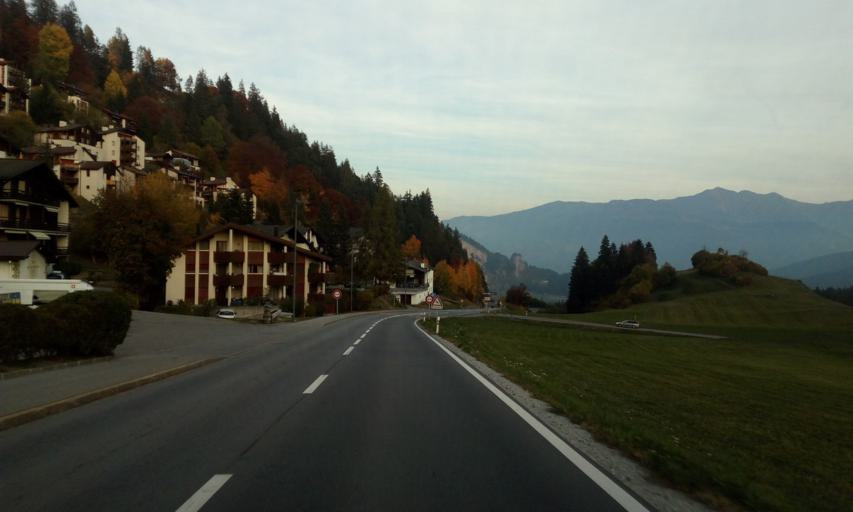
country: CH
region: Grisons
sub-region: Imboden District
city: Flims
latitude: 46.8351
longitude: 9.2991
